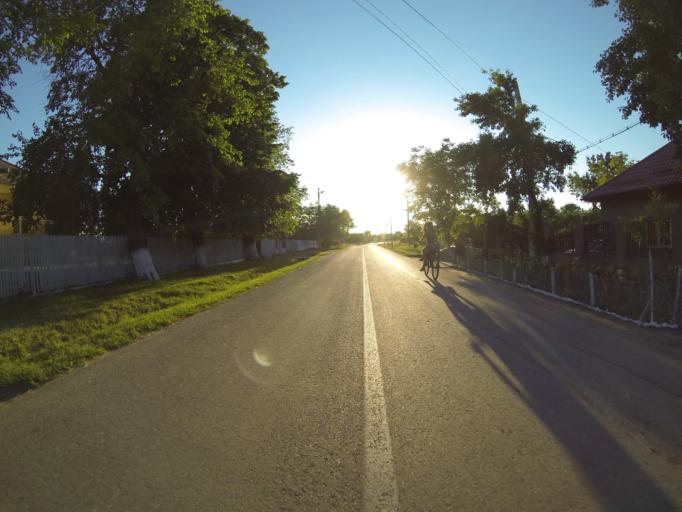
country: RO
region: Dolj
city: Satu Nou Calopar
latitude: 44.1625
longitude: 23.7646
